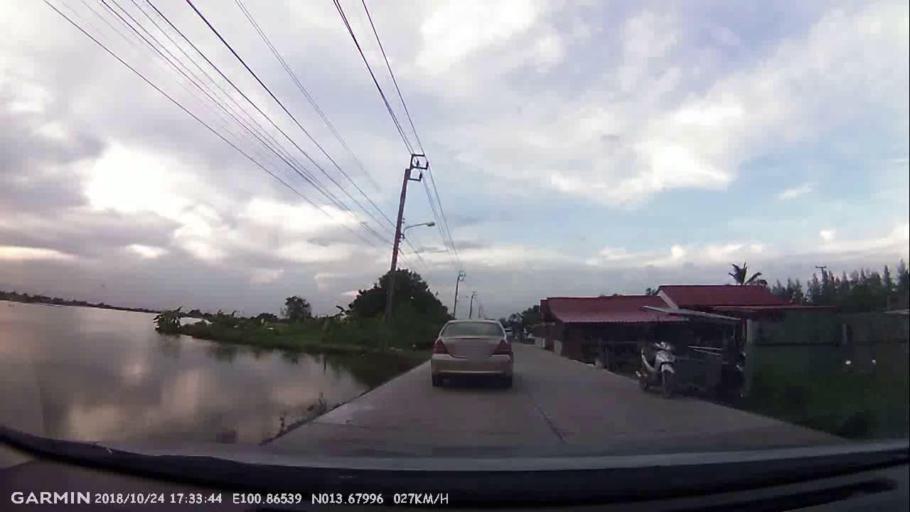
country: TH
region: Samut Prakan
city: Ban Khlong Bang Sao Thong
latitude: 13.6800
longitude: 100.8654
